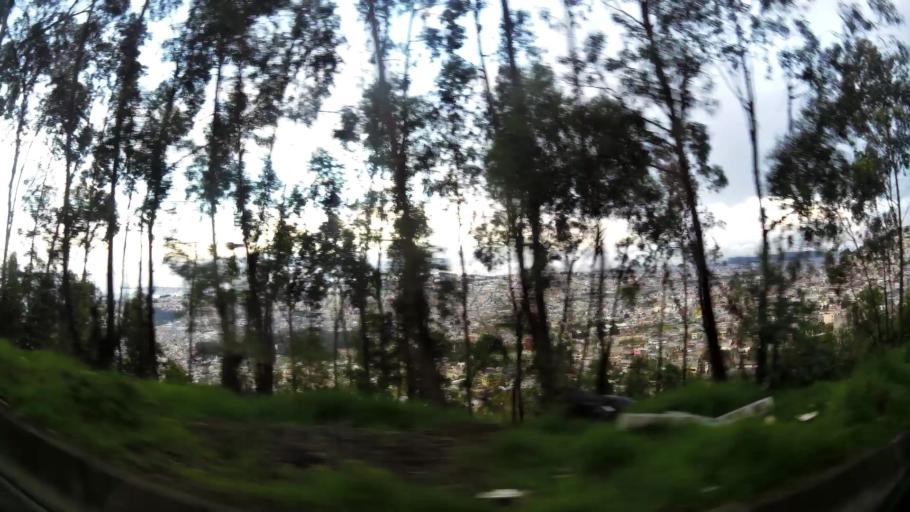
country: EC
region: Pichincha
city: Quito
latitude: -0.1143
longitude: -78.5128
